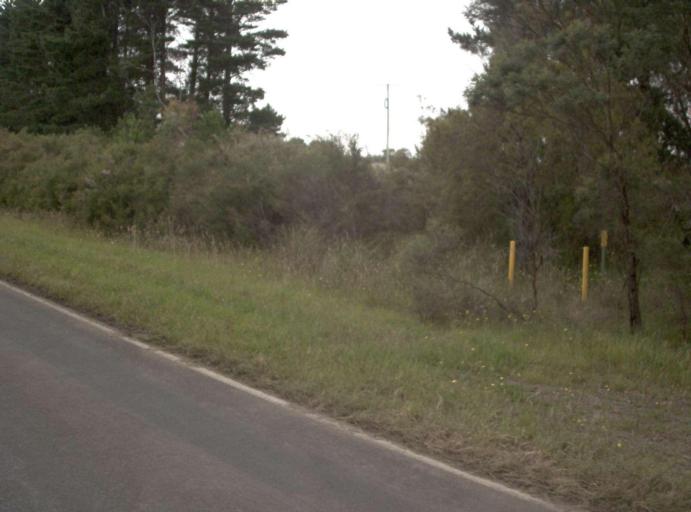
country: AU
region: Victoria
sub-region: Latrobe
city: Traralgon
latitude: -38.5543
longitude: 146.7601
